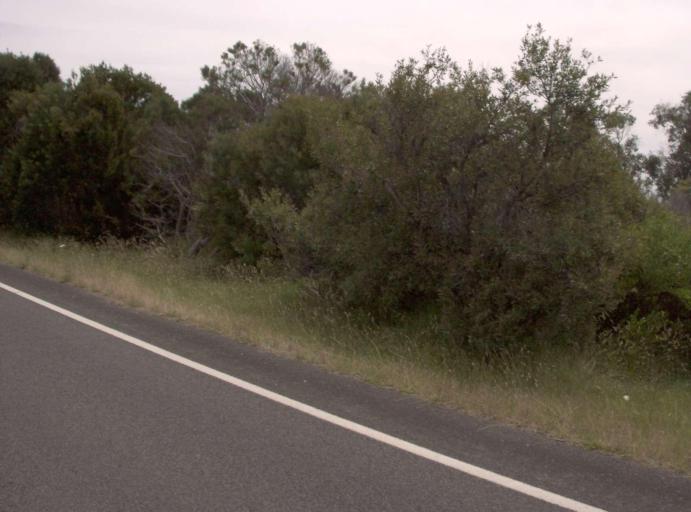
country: AU
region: Victoria
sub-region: Mornington Peninsula
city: Safety Beach
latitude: -38.3292
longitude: 144.9904
